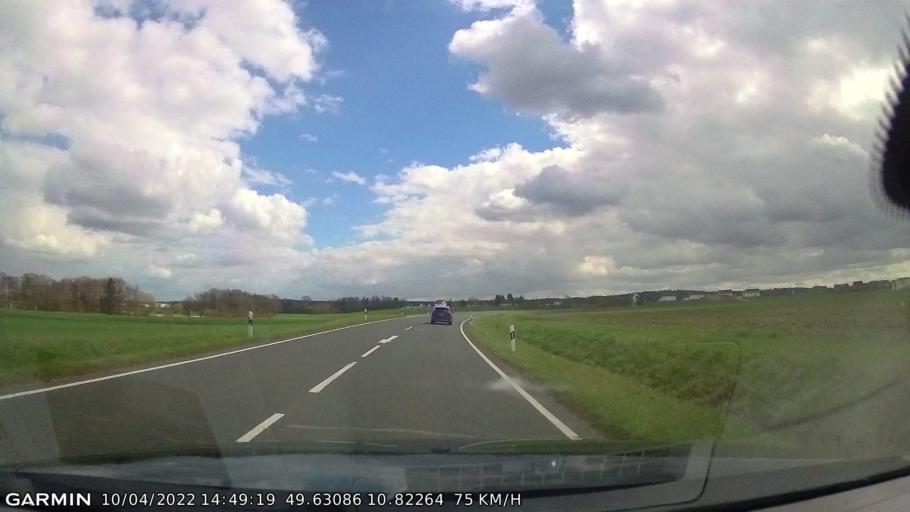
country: DE
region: Bavaria
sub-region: Regierungsbezirk Mittelfranken
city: Weisendorf
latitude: 49.6309
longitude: 10.8228
